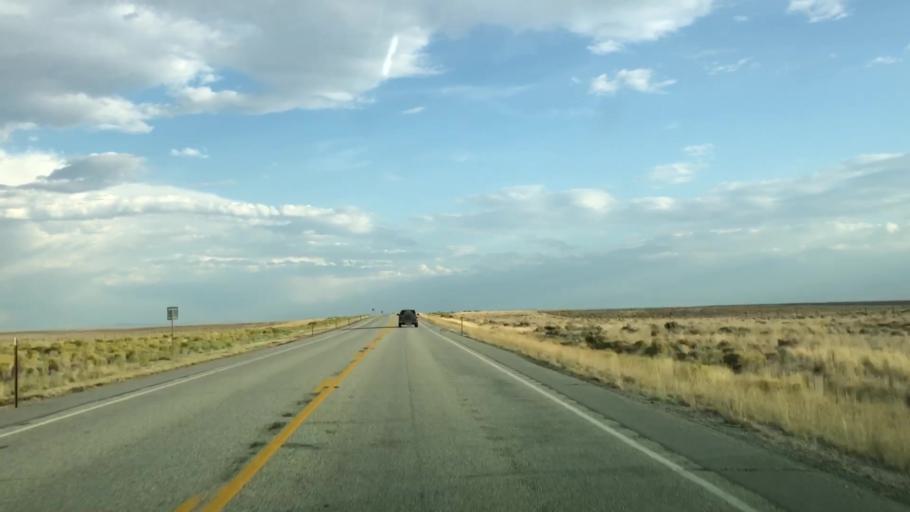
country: US
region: Wyoming
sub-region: Sublette County
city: Marbleton
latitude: 42.3224
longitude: -109.5100
